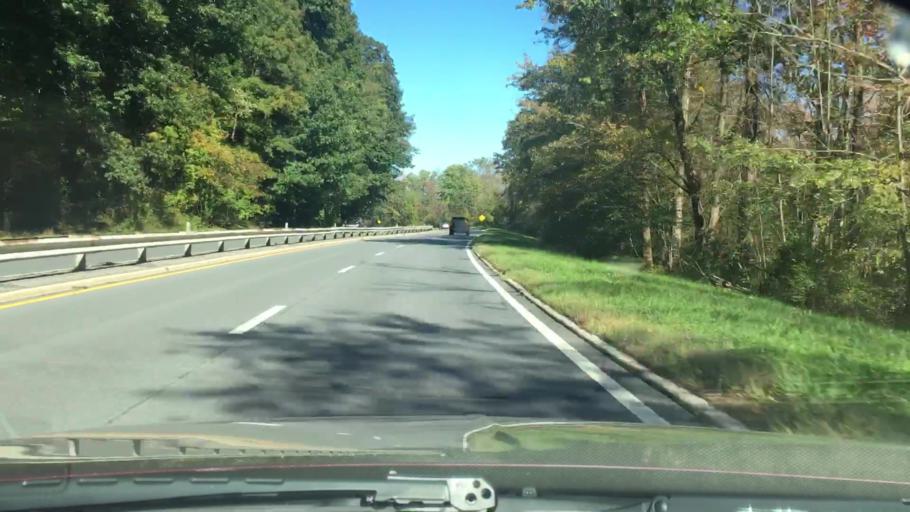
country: US
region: New York
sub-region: Westchester County
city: Mount Kisco
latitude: 41.1930
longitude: -73.7479
